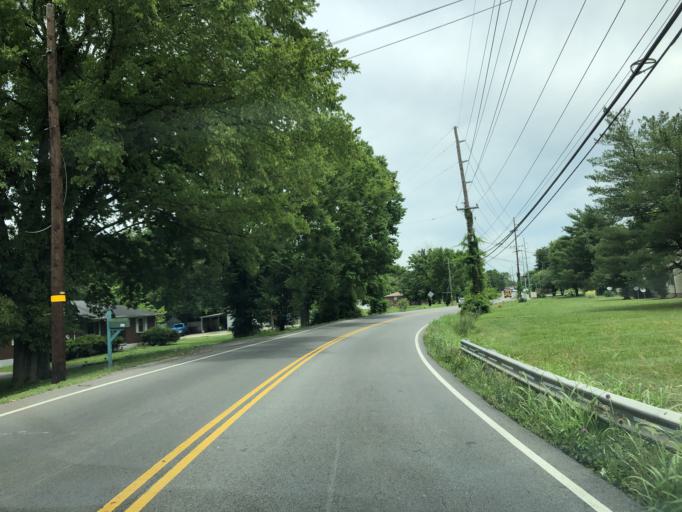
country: US
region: Tennessee
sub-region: Davidson County
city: Nashville
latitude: 36.2449
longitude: -86.7802
